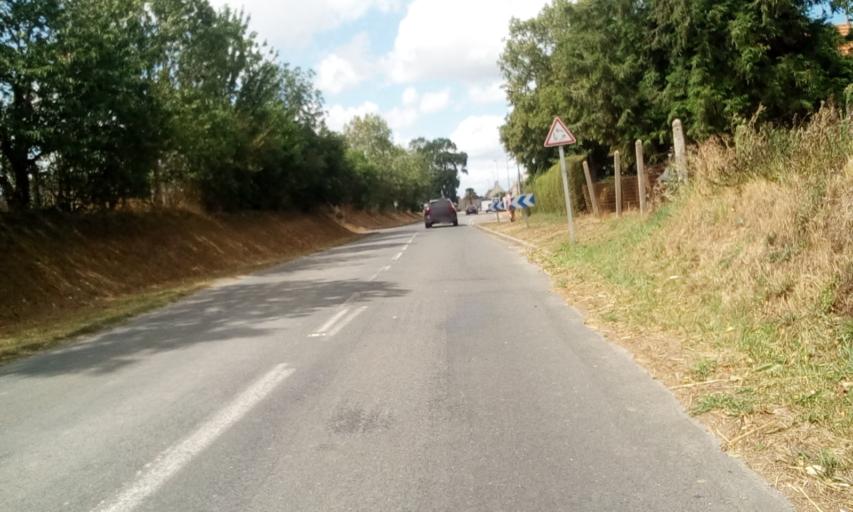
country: FR
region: Lower Normandy
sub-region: Departement du Calvados
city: Creully
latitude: 49.2835
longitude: -0.5324
